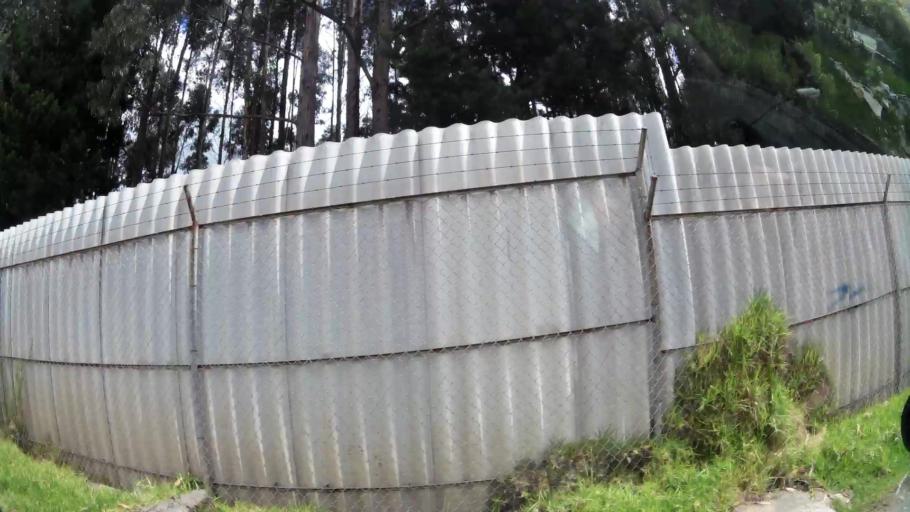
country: EC
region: Pichincha
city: Sangolqui
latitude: -0.3429
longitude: -78.5444
